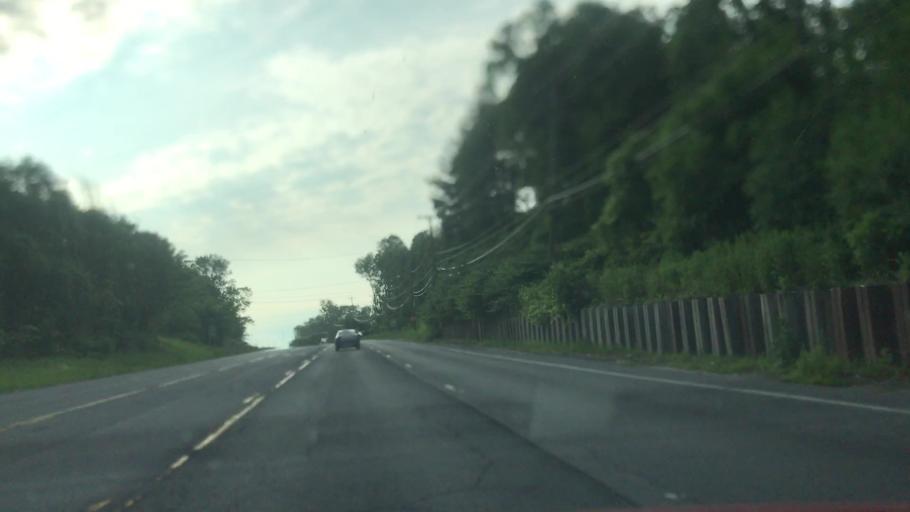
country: US
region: New York
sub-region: Albany County
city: Watervliet
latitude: 42.7355
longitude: -73.7208
